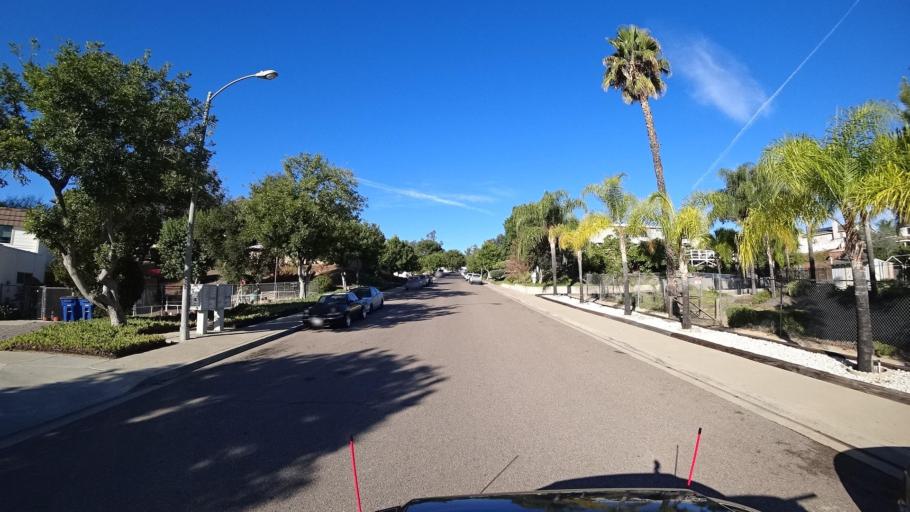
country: US
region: California
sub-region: San Diego County
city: Lakeside
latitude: 32.8475
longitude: -116.9080
